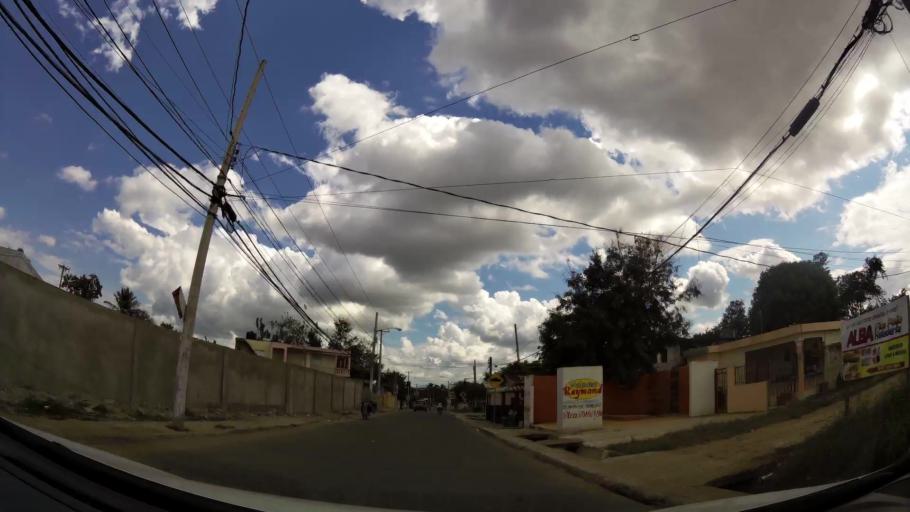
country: DO
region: Santiago
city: Licey al Medio
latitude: 19.3980
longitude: -70.6492
